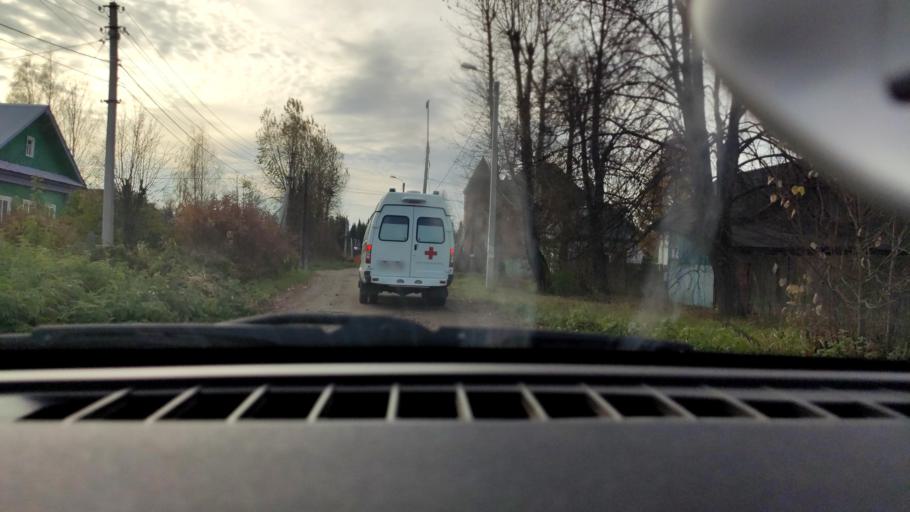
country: RU
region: Perm
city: Froly
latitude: 57.9760
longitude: 56.3101
